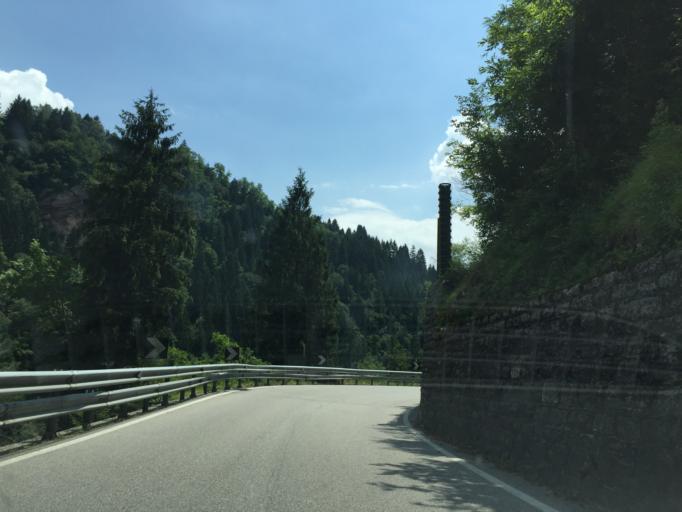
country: IT
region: Veneto
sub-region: Provincia di Belluno
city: Lamon
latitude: 46.0521
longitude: 11.7635
